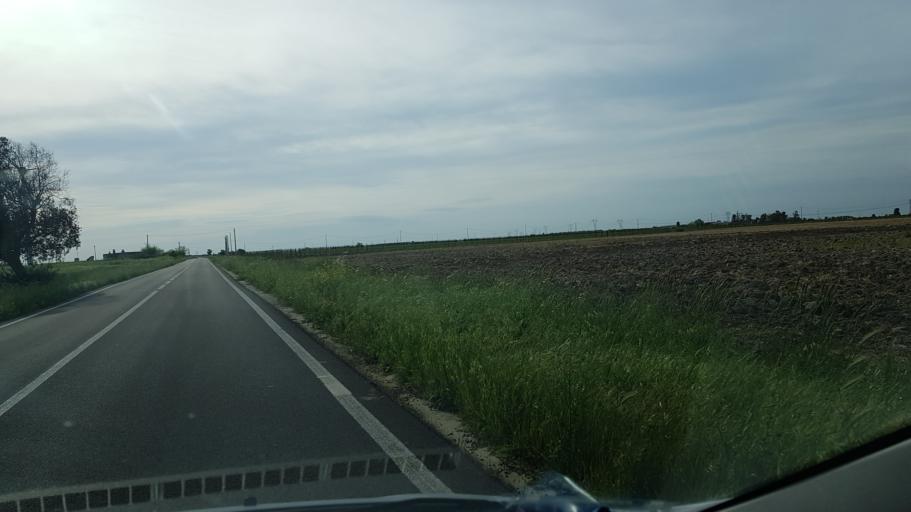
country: IT
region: Apulia
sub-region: Provincia di Brindisi
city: Tuturano
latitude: 40.5287
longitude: 17.9029
